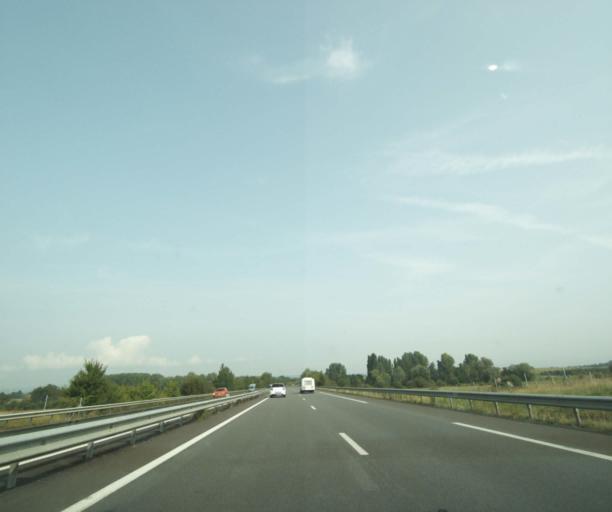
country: FR
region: Pays de la Loire
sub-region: Departement de la Sarthe
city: Saint-Paterne
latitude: 48.4342
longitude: 0.1370
